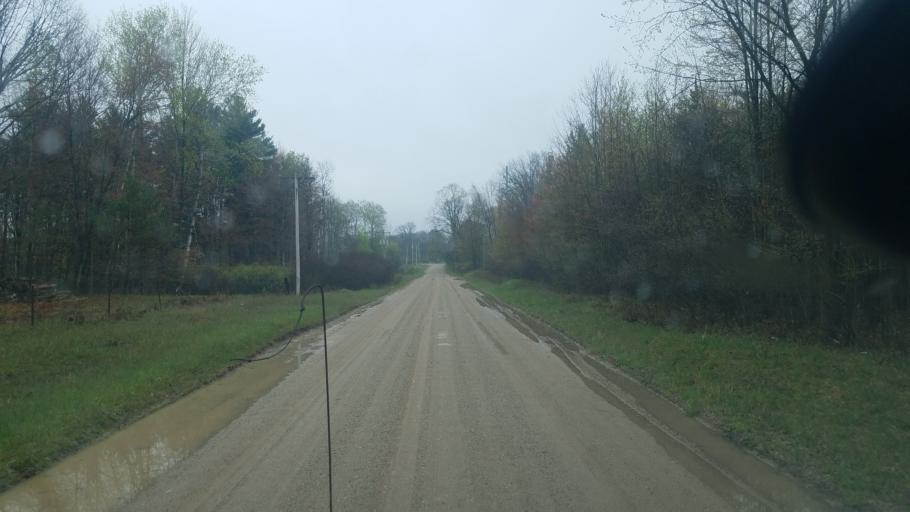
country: US
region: Michigan
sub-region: Montcalm County
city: Lakeview
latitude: 43.4678
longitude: -85.2985
